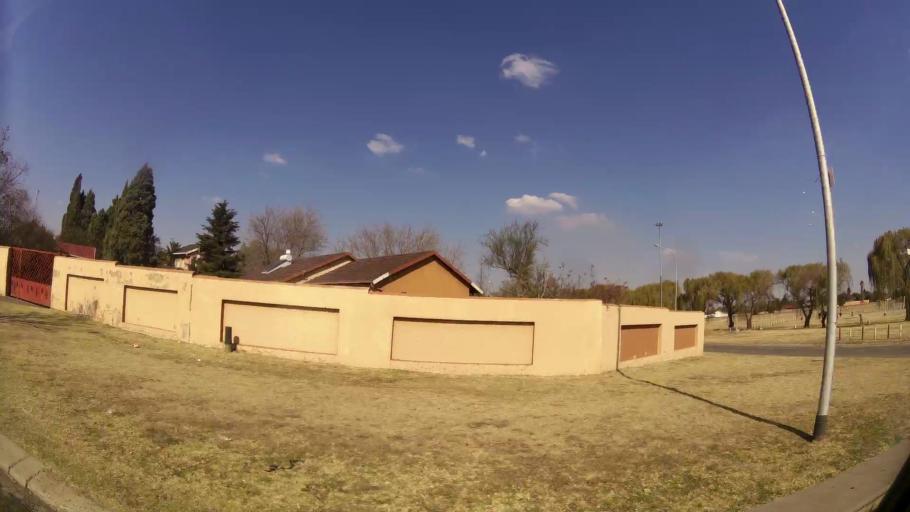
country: ZA
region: Gauteng
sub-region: Ekurhuleni Metropolitan Municipality
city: Benoni
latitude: -26.2463
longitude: 28.3105
